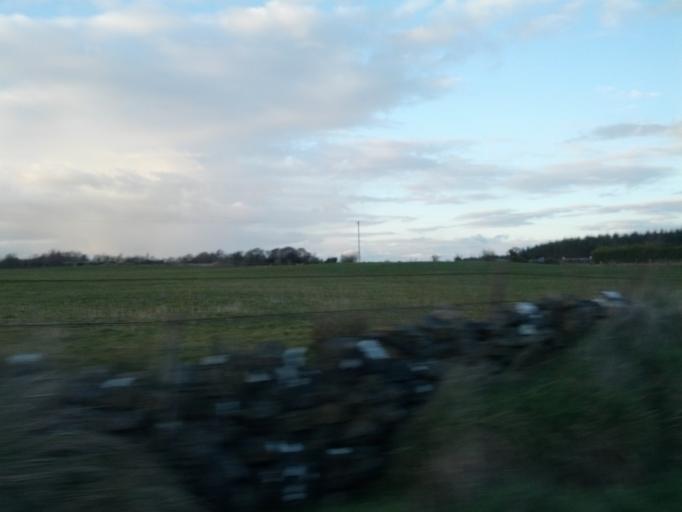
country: IE
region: Connaught
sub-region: County Galway
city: Athenry
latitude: 53.3247
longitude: -8.6672
